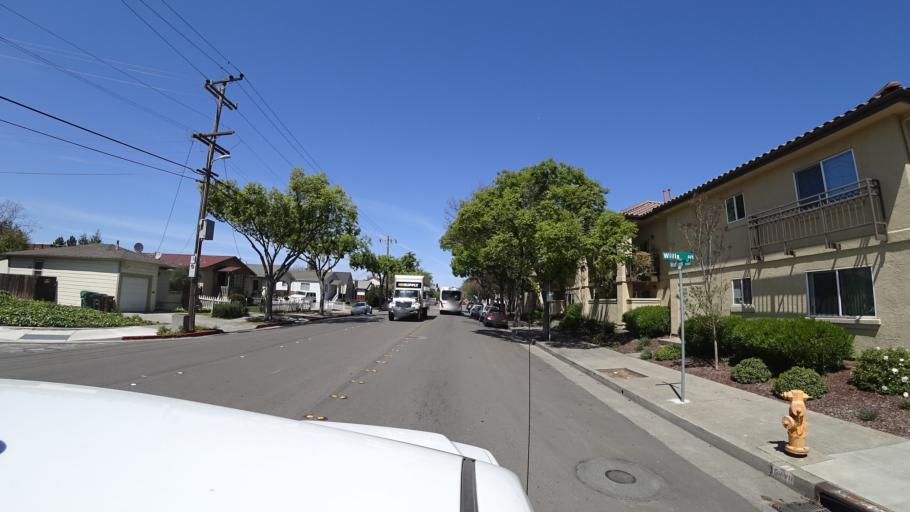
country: US
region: California
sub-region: Alameda County
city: Hayward
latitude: 37.6684
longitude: -122.0821
